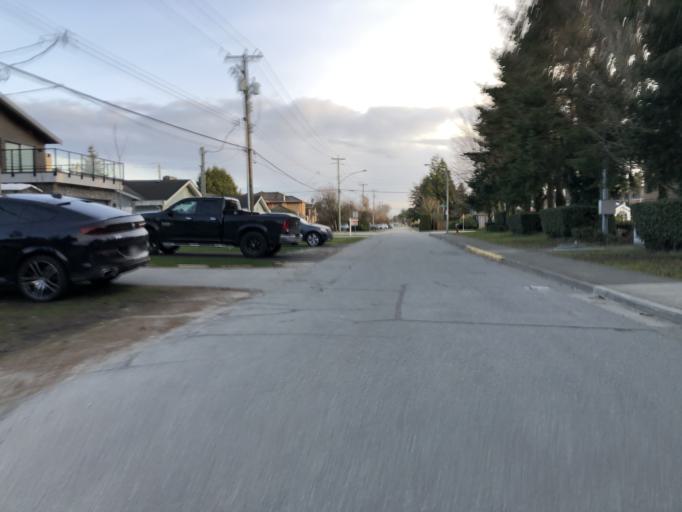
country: CA
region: British Columbia
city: Richmond
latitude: 49.1544
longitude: -123.1226
